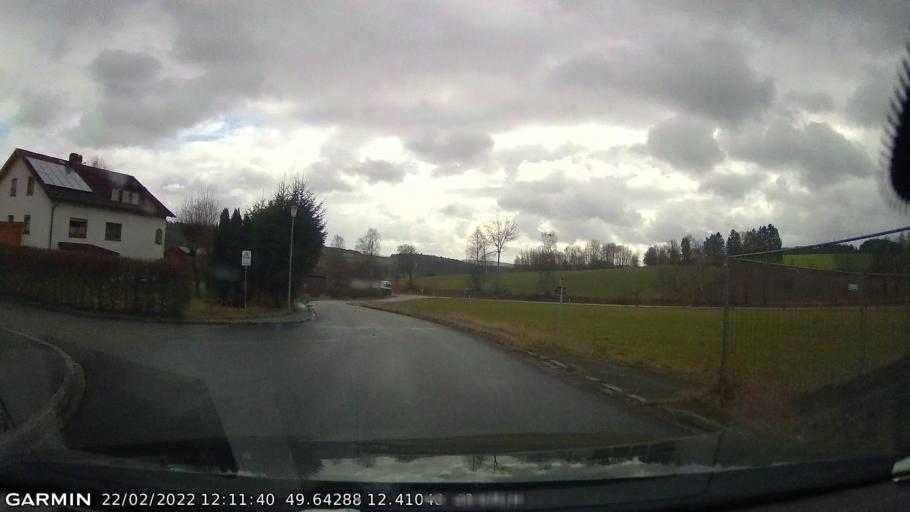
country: DE
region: Bavaria
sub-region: Upper Palatinate
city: Pleystein
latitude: 49.6429
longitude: 12.4105
